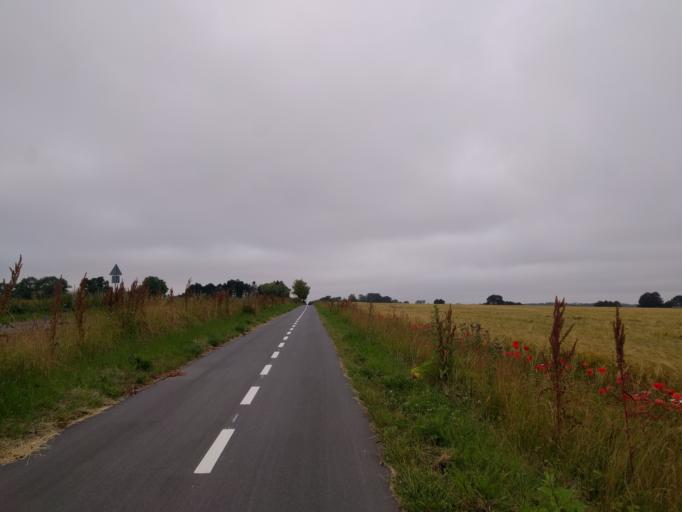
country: DK
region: South Denmark
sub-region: Kerteminde Kommune
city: Langeskov
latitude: 55.4049
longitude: 10.5733
